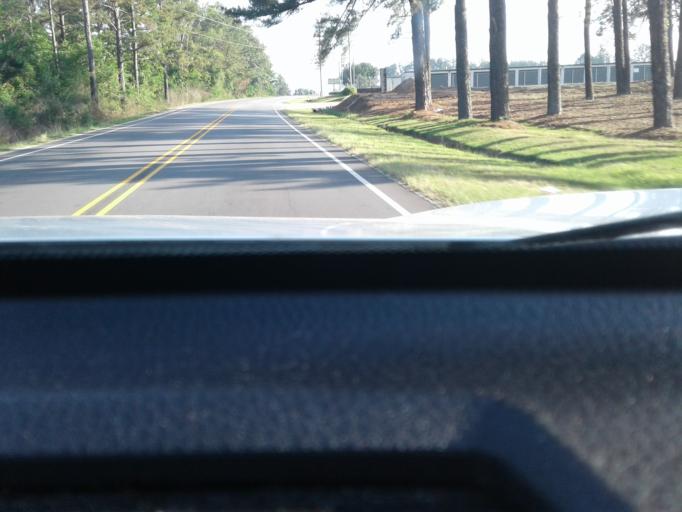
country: US
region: North Carolina
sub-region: Harnett County
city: Dunn
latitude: 35.3225
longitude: -78.6309
